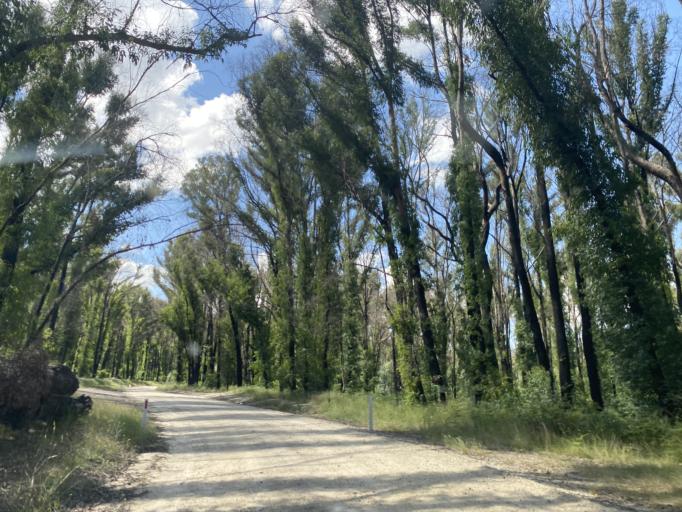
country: AU
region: Victoria
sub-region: Cardinia
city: Gembrook
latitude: -37.9861
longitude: 145.6519
